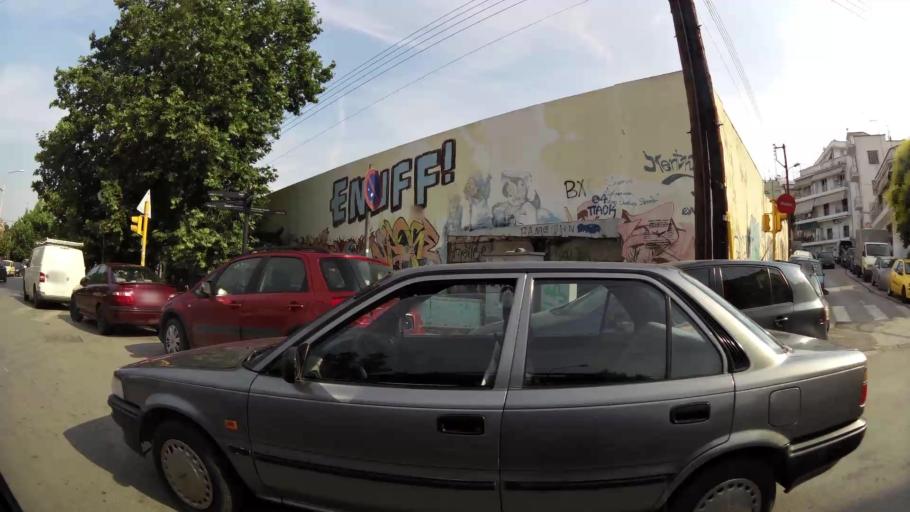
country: GR
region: Central Macedonia
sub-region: Nomos Thessalonikis
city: Thessaloniki
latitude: 40.6447
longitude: 22.9402
